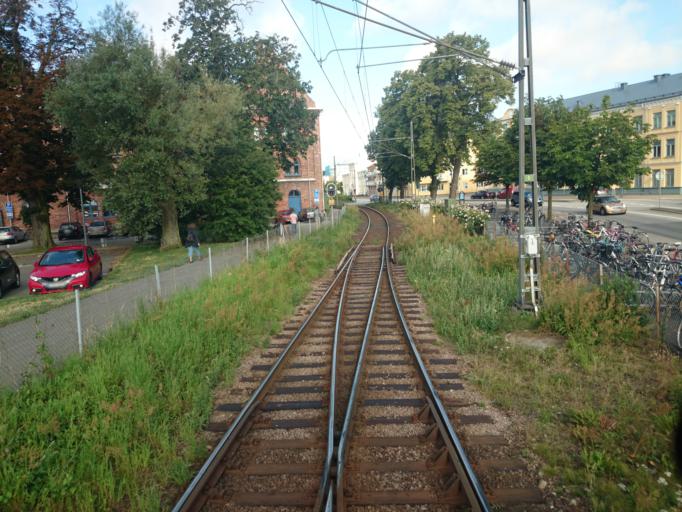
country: SE
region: Skane
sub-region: Ystads Kommun
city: Ystad
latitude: 55.4274
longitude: 13.8235
